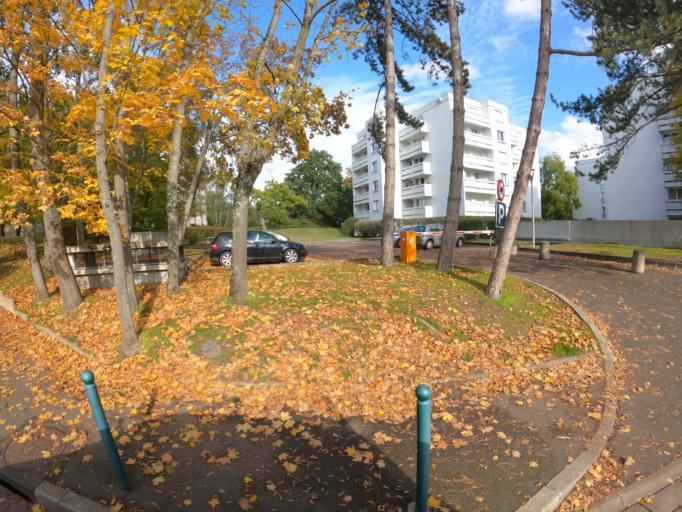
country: FR
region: Ile-de-France
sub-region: Departement de Seine-et-Marne
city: Vaires-sur-Marne
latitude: 48.8766
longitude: 2.6406
